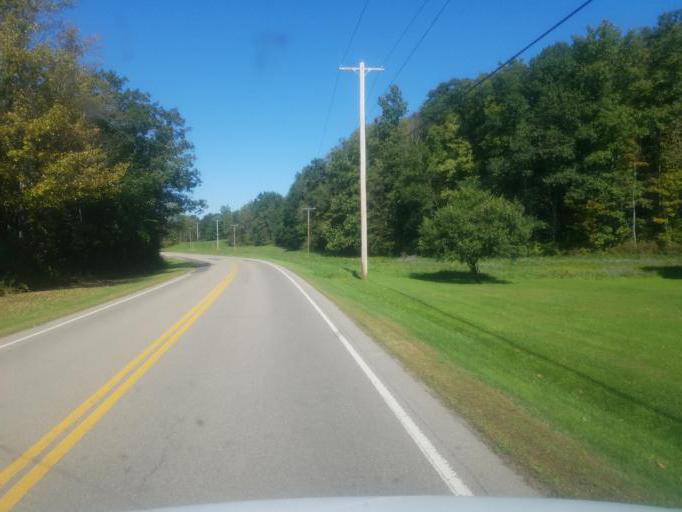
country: US
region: New York
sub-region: Allegany County
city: Friendship
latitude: 42.3105
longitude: -78.1074
